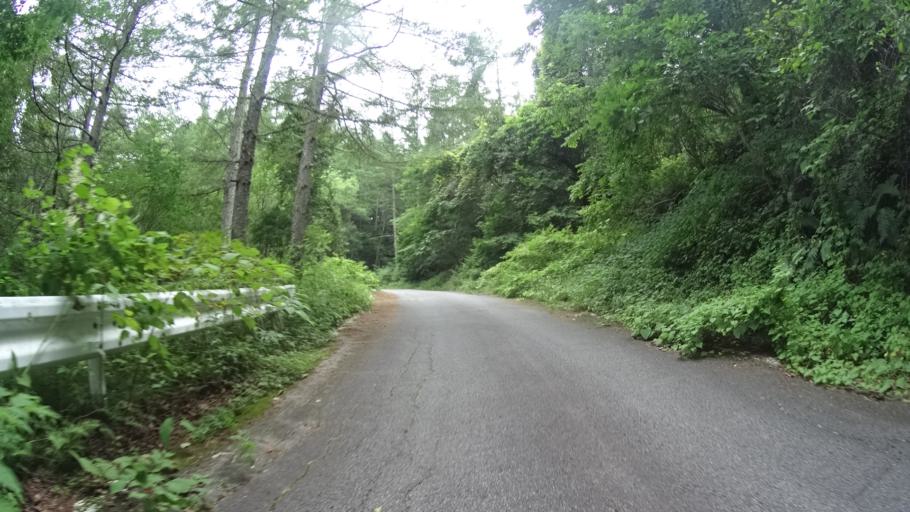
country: JP
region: Yamanashi
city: Enzan
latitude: 35.8048
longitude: 138.6331
